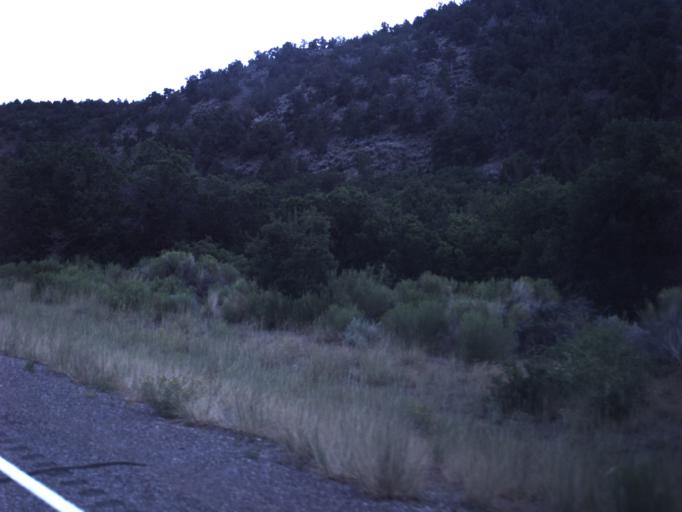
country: US
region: Utah
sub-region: Sevier County
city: Richfield
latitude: 38.7416
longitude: -111.9221
